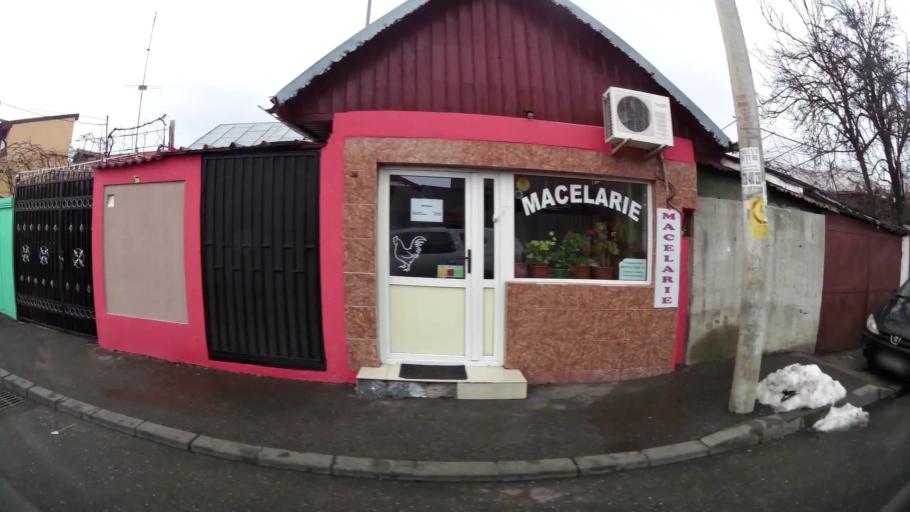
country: RO
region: Ilfov
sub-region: Comuna Pantelimon
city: Pantelimon
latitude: 44.4304
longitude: 26.2042
